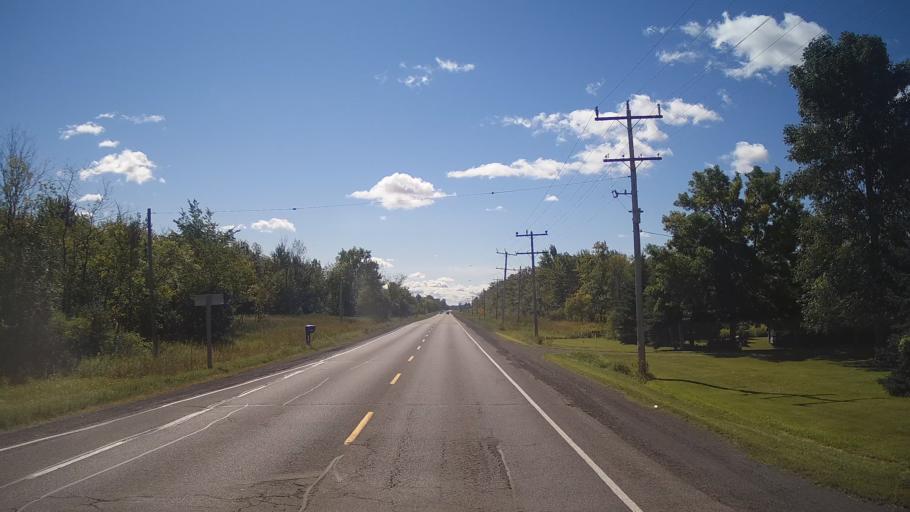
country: US
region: New York
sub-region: St. Lawrence County
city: Norfolk
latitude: 44.9519
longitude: -75.2252
